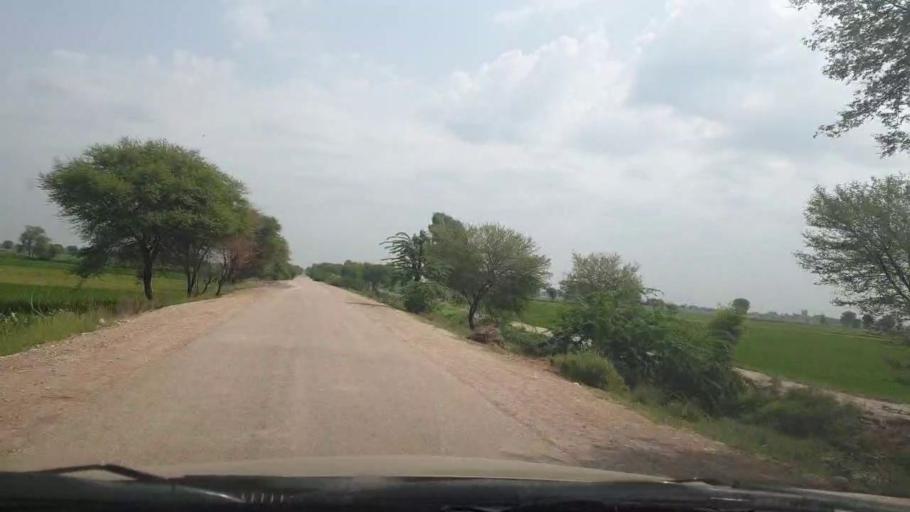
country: PK
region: Sindh
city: Miro Khan
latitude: 27.6864
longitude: 68.1911
